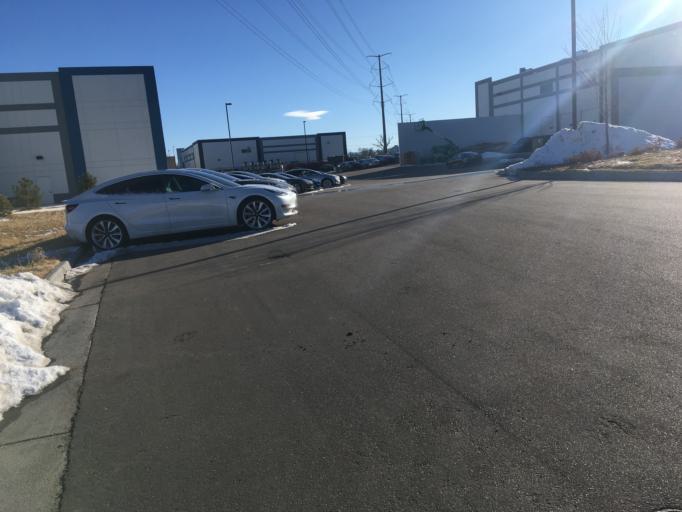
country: US
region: Colorado
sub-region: Adams County
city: Twin Lakes
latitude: 39.7910
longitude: -104.9807
